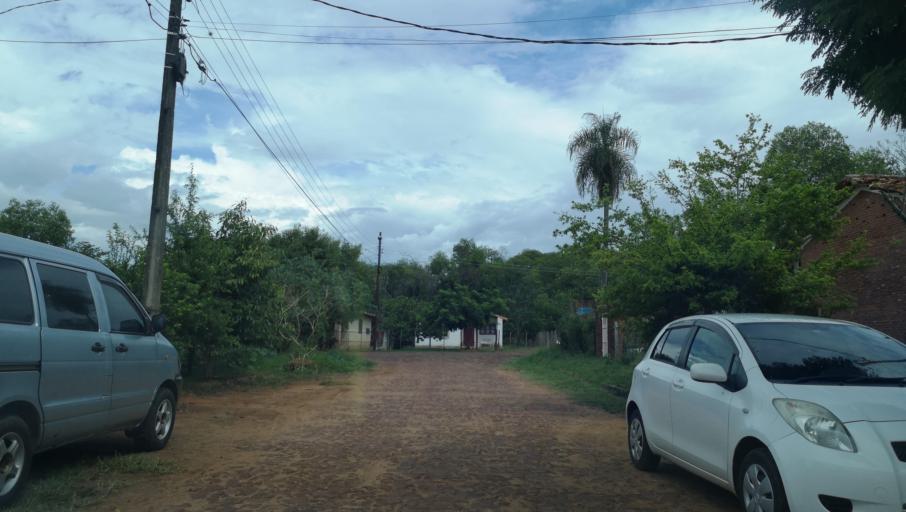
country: PY
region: Misiones
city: Santa Maria
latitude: -26.8800
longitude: -57.0266
